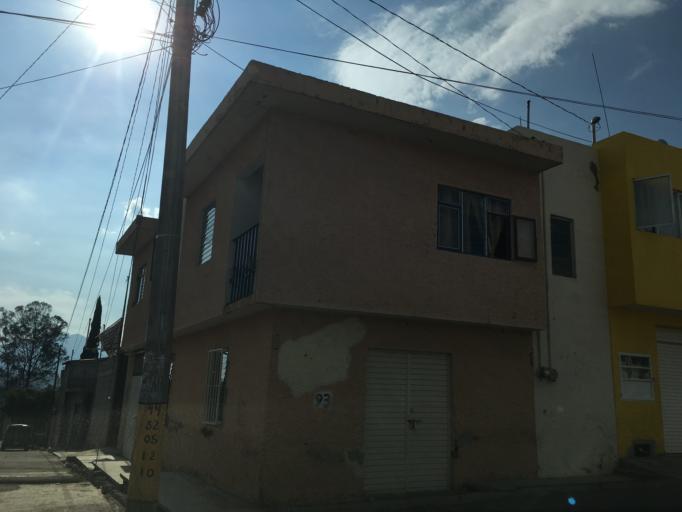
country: MX
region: Michoacan
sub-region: Morelia
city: Morelos
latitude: 19.6435
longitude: -101.2374
